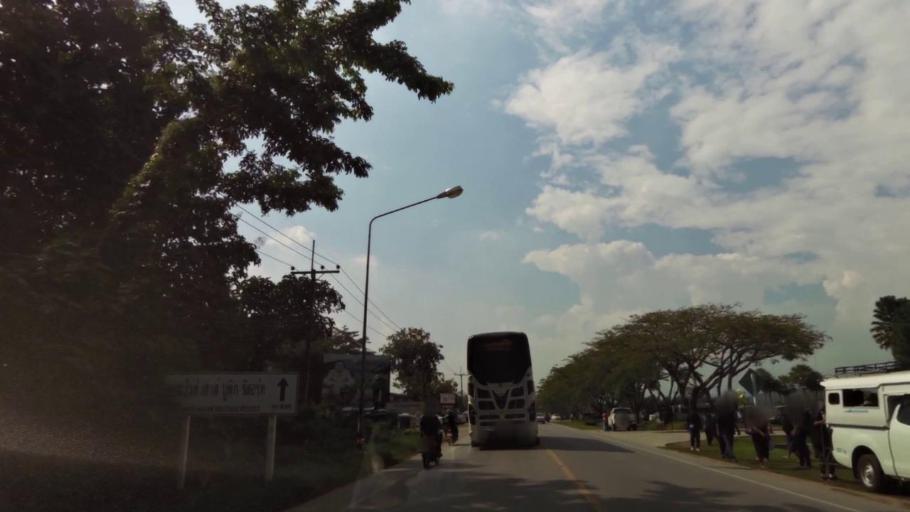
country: TH
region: Chiang Rai
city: Mae Lao
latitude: 19.8530
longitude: 99.7455
